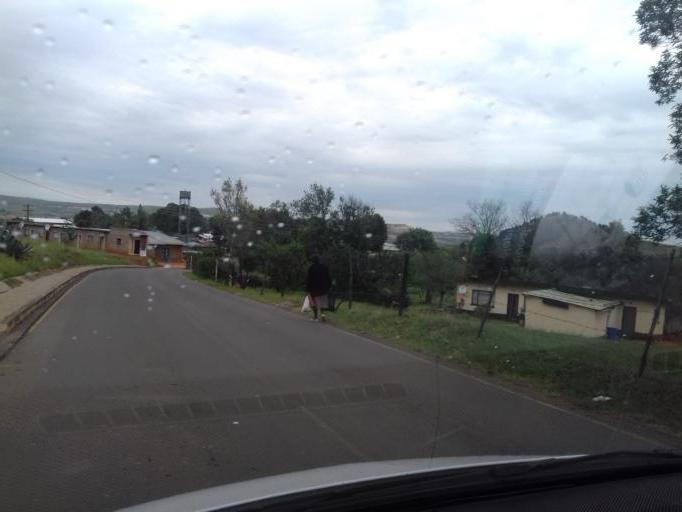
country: LS
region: Berea
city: Teyateyaneng
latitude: -29.1036
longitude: 27.9582
